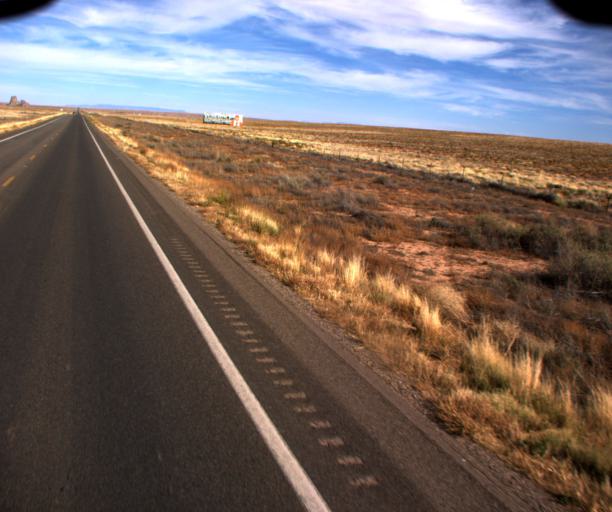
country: US
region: Arizona
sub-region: Navajo County
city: Kayenta
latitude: 36.7136
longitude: -110.2091
